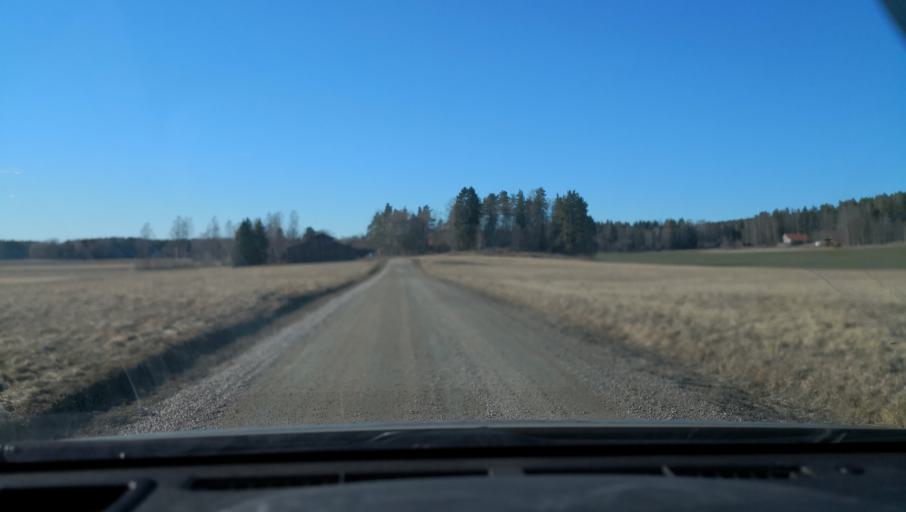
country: SE
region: Vaestmanland
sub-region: Sala Kommun
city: Sala
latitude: 60.1496
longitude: 16.6398
